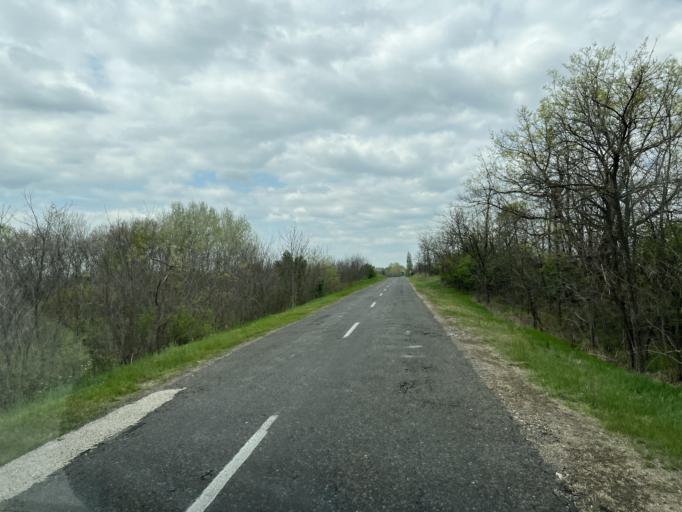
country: HU
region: Pest
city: Dabas
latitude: 47.1277
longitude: 19.3455
